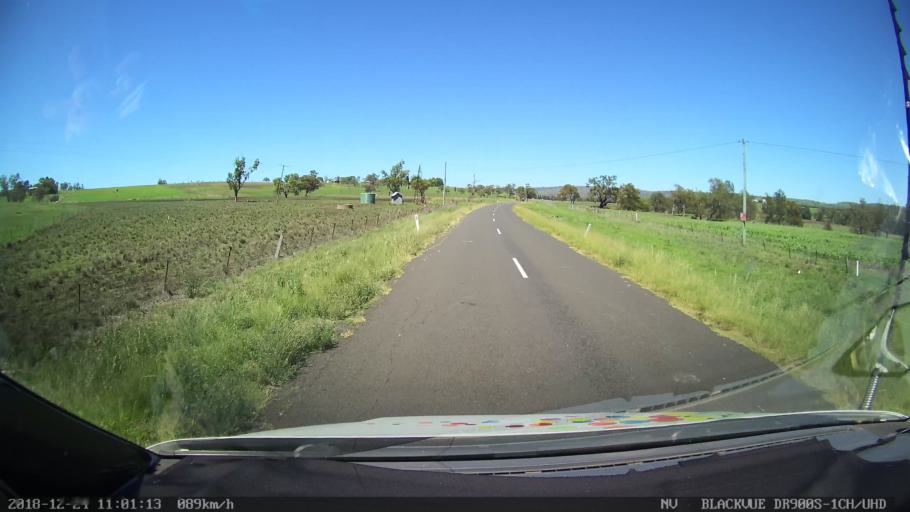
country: AU
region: New South Wales
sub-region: Upper Hunter Shire
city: Merriwa
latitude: -32.0749
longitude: 150.3867
